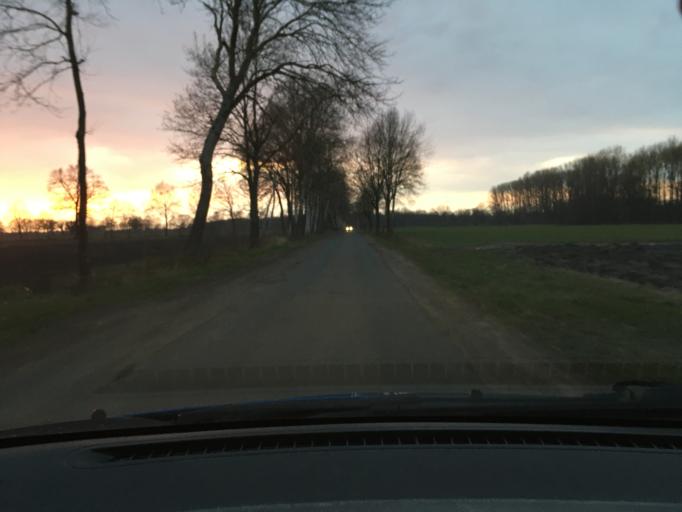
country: DE
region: Lower Saxony
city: Neetze
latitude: 53.3020
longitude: 10.6679
